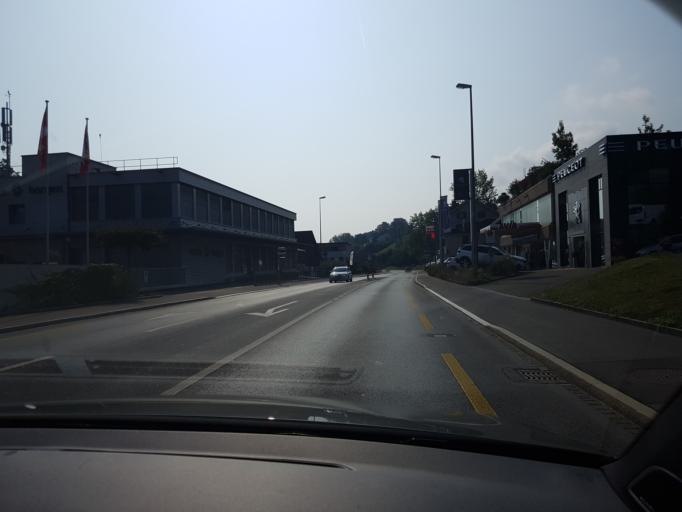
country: CH
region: Zurich
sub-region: Bezirk Horgen
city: Horgen / Allmend
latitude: 47.2536
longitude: 8.6188
